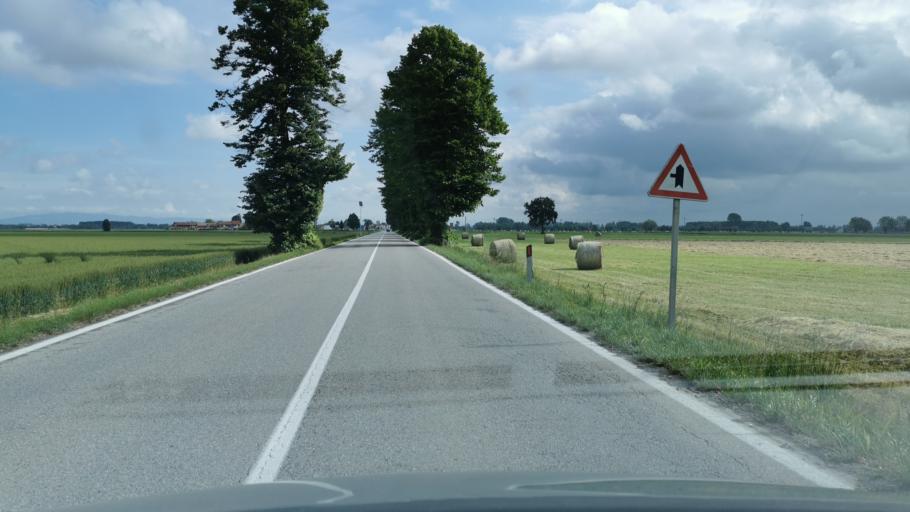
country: IT
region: Piedmont
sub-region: Provincia di Cuneo
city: Racconigi
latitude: 44.8083
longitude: 7.6964
